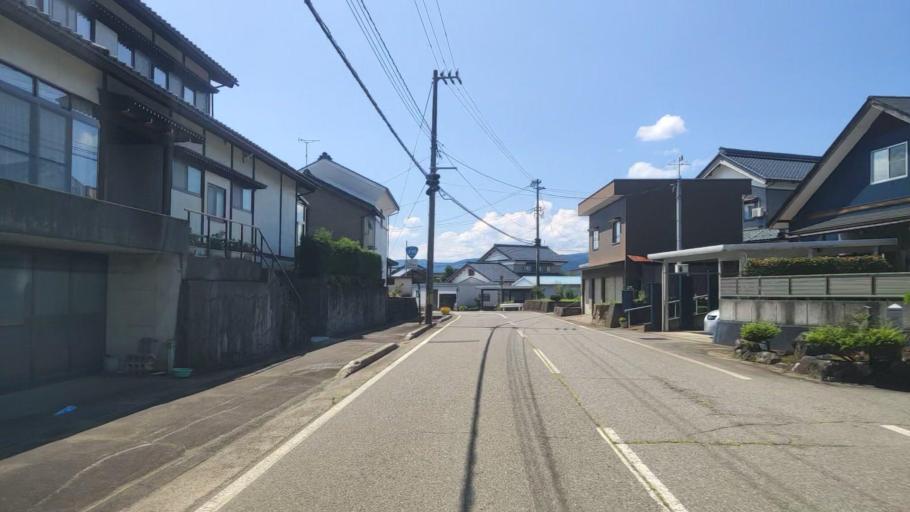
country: JP
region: Fukui
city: Katsuyama
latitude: 36.0920
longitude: 136.4910
